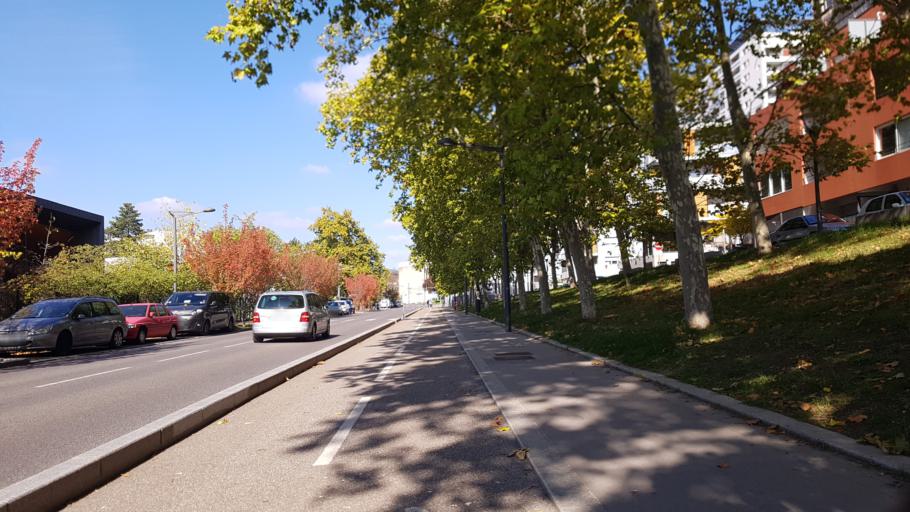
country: FR
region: Rhone-Alpes
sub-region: Departement du Rhone
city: Ecully
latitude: 45.7873
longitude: 4.7932
